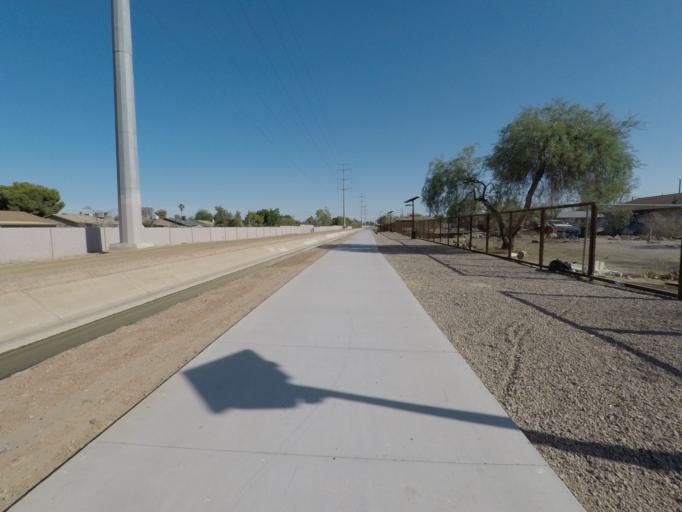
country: US
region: Arizona
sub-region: Maricopa County
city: Guadalupe
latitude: 33.3667
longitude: -111.9570
